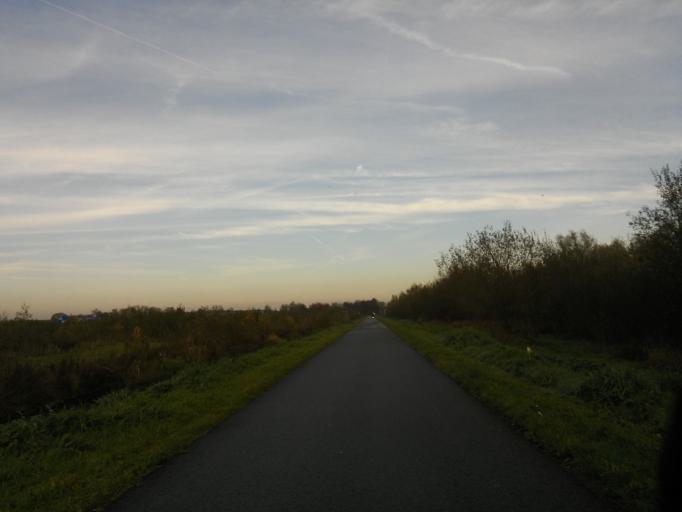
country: NL
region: Utrecht
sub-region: Gemeente Amersfoort
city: Randenbroek
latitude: 52.1560
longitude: 5.4191
